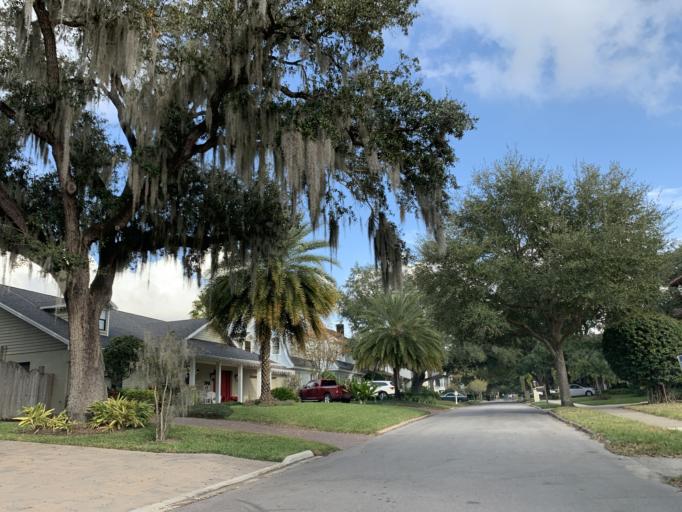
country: US
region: Florida
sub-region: Hillsborough County
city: Tampa
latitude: 27.9079
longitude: -82.4966
